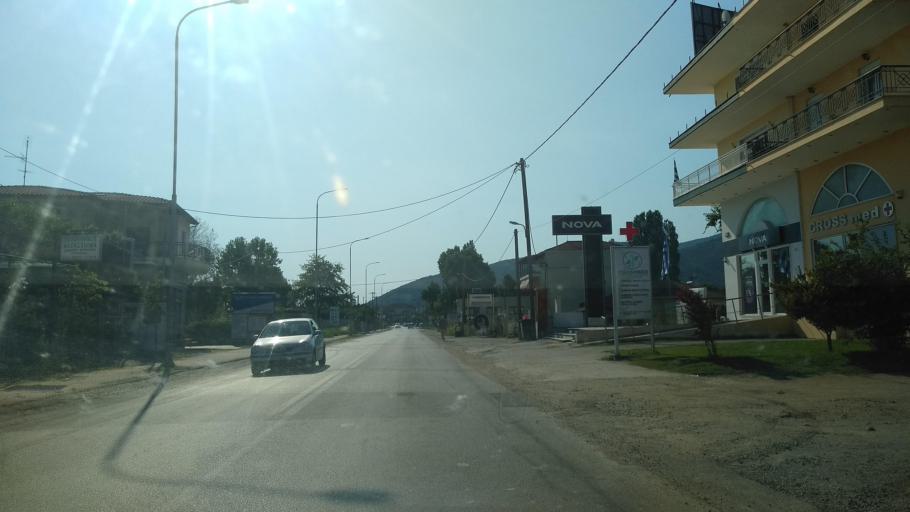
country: GR
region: Central Macedonia
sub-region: Nomos Thessalonikis
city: Stavros
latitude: 40.6662
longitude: 23.6874
